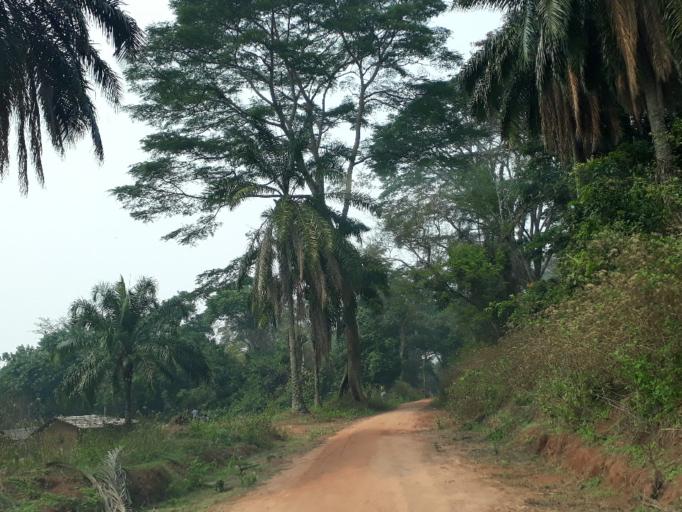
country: CD
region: Kasai-Occidental
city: Tshikapa
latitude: -6.1650
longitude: 20.4226
